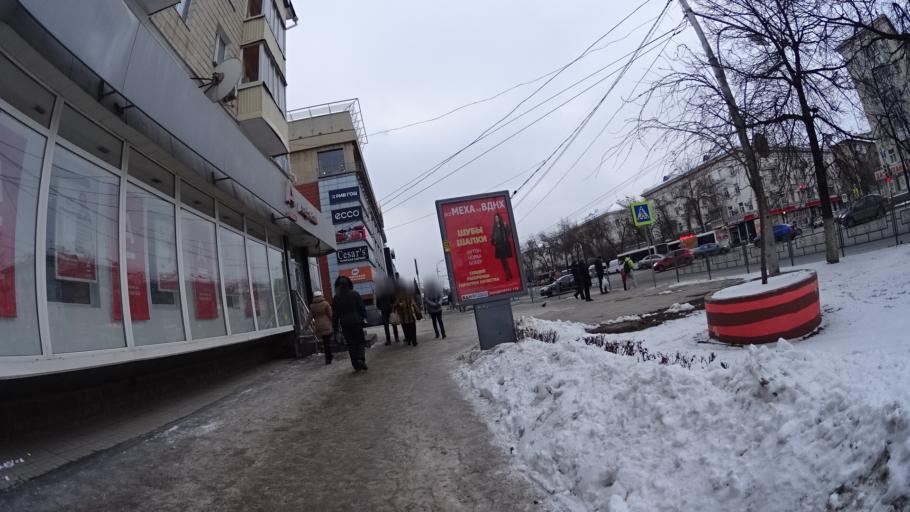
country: RU
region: Bashkortostan
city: Ufa
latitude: 54.7423
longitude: 55.9895
